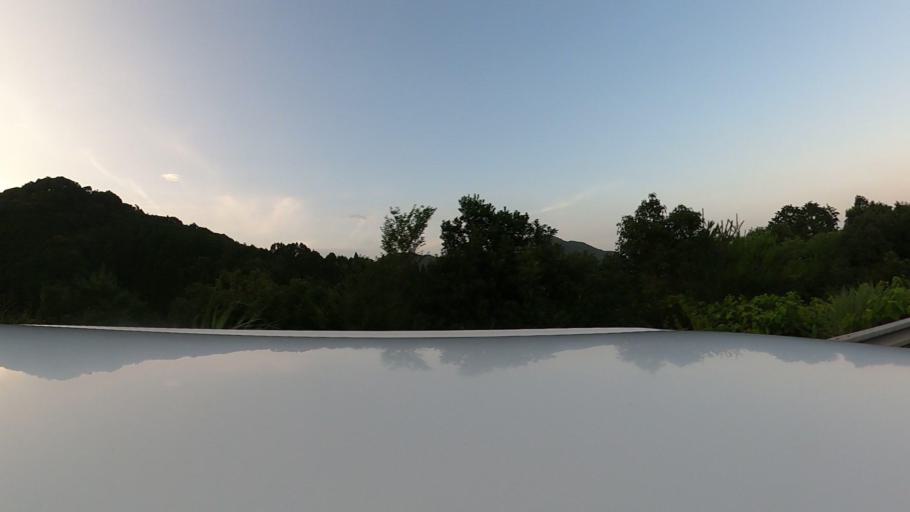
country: JP
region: Miyazaki
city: Nobeoka
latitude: 32.5450
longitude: 131.6478
